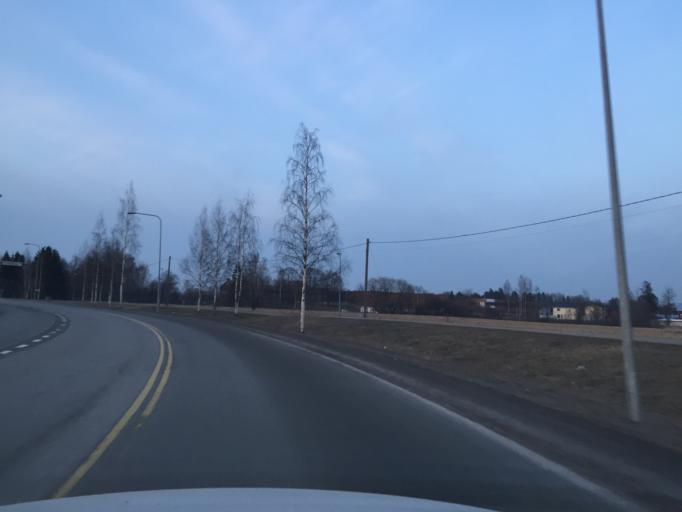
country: FI
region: Uusimaa
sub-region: Helsinki
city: Vantaa
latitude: 60.2674
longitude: 24.9746
